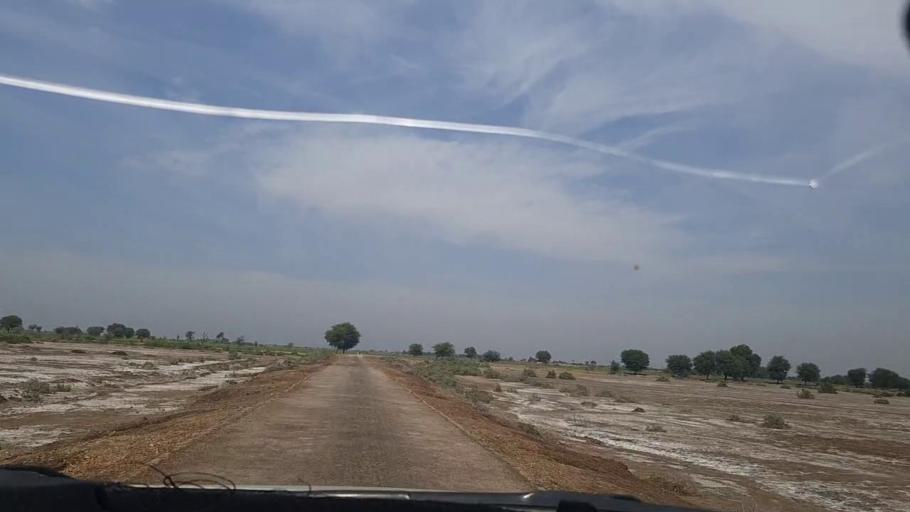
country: PK
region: Sindh
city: Pithoro
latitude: 25.4543
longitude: 69.4645
